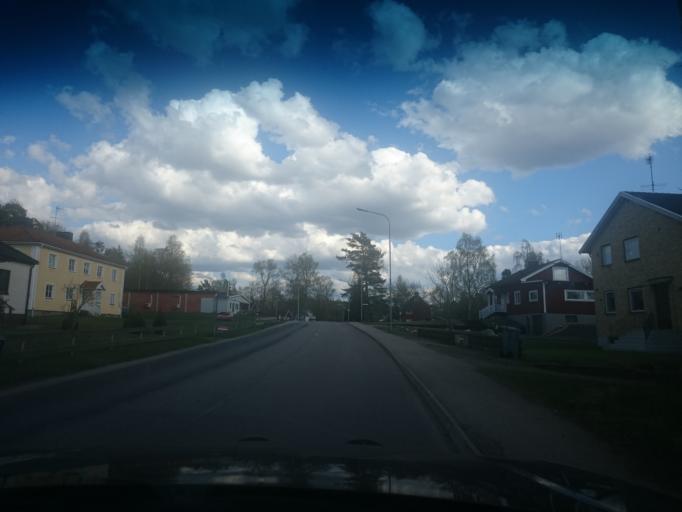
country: SE
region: Kronoberg
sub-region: Vaxjo Kommun
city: Braas
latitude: 57.1373
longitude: 15.1404
